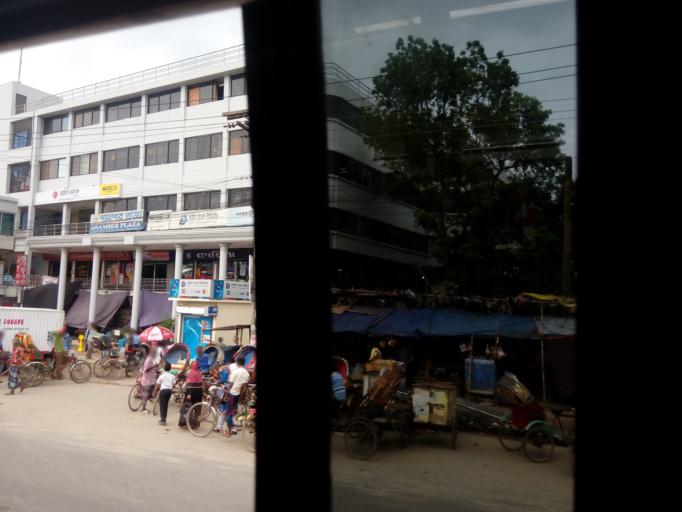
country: BD
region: Dhaka
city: Tungi
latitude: 23.9534
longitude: 90.2732
